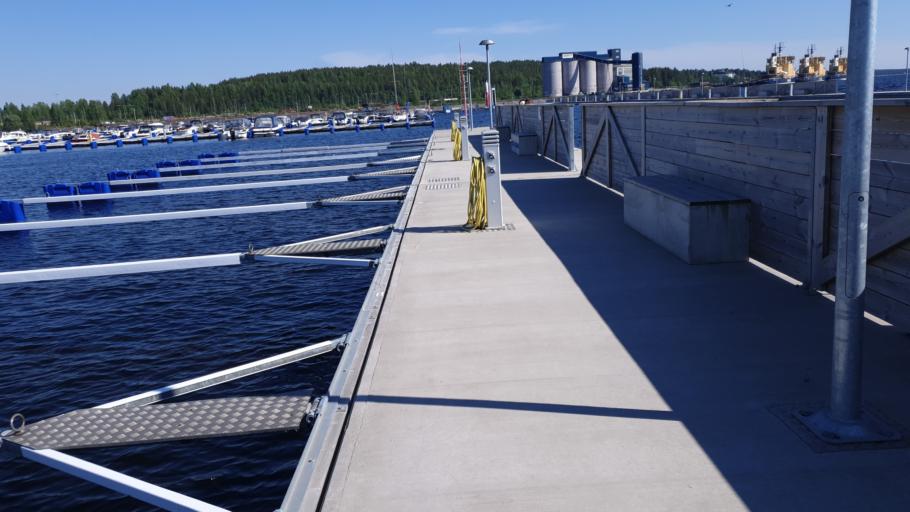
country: SE
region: Norrbotten
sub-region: Lulea Kommun
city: Lulea
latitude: 65.5784
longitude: 22.1621
